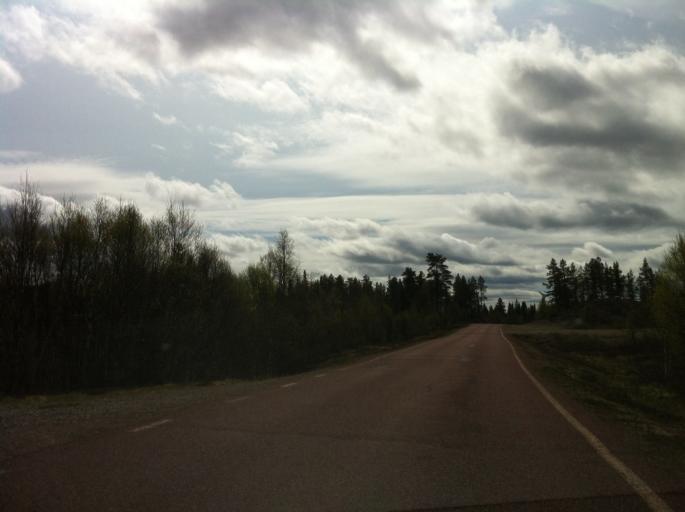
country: NO
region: Hedmark
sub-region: Engerdal
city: Engerdal
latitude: 62.1619
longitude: 12.9425
